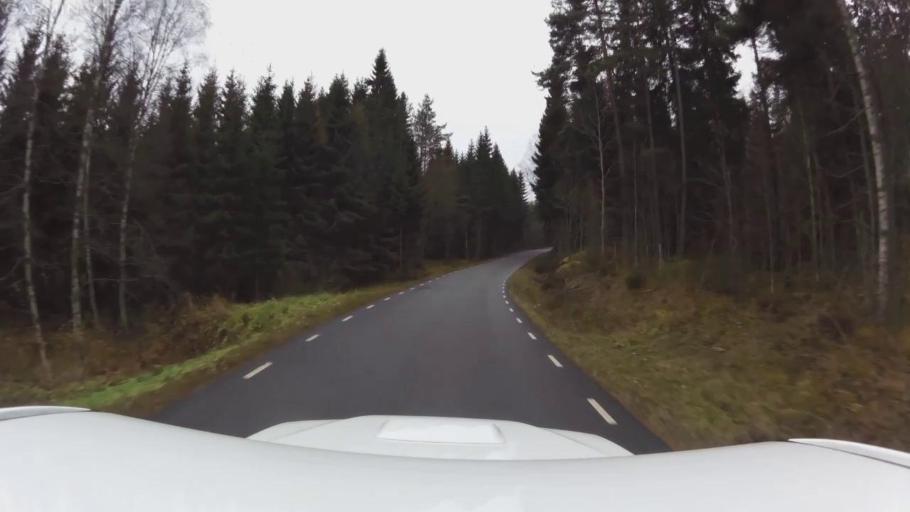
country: SE
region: OEstergoetland
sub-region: Mjolby Kommun
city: Mantorp
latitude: 58.1734
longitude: 15.3977
